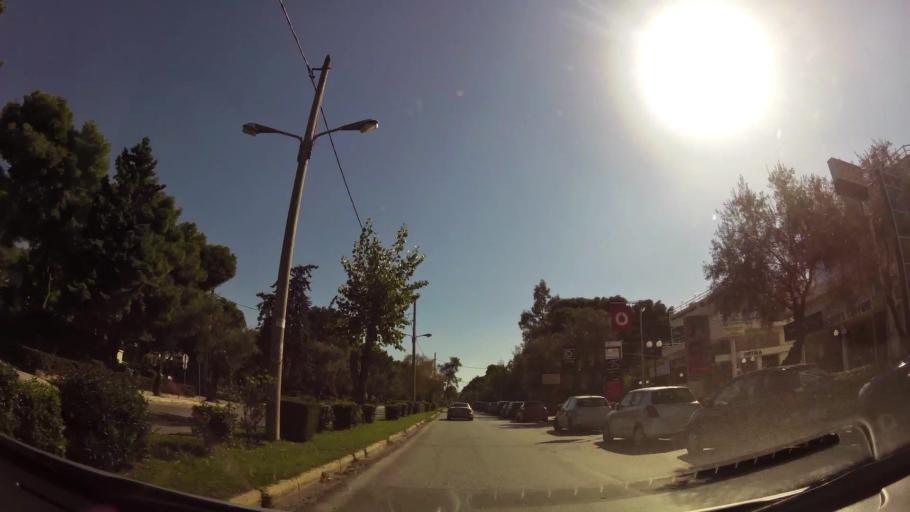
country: GR
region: Attica
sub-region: Nomarchia Athinas
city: Kifisia
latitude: 38.0902
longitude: 23.7975
